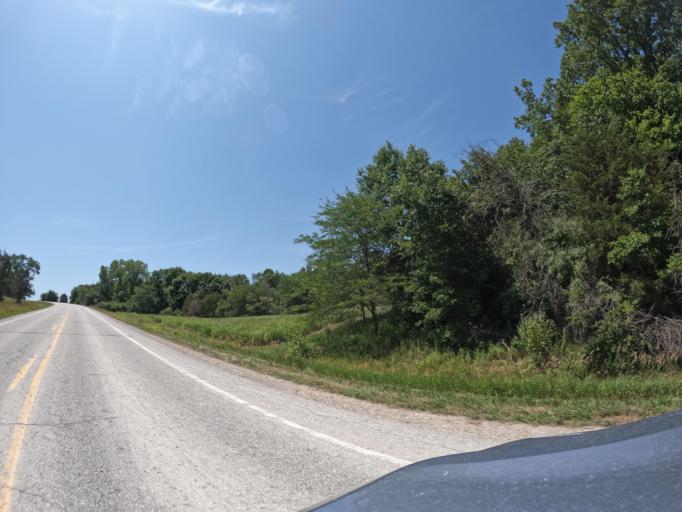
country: US
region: Iowa
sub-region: Henry County
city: Mount Pleasant
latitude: 40.9327
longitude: -91.6211
